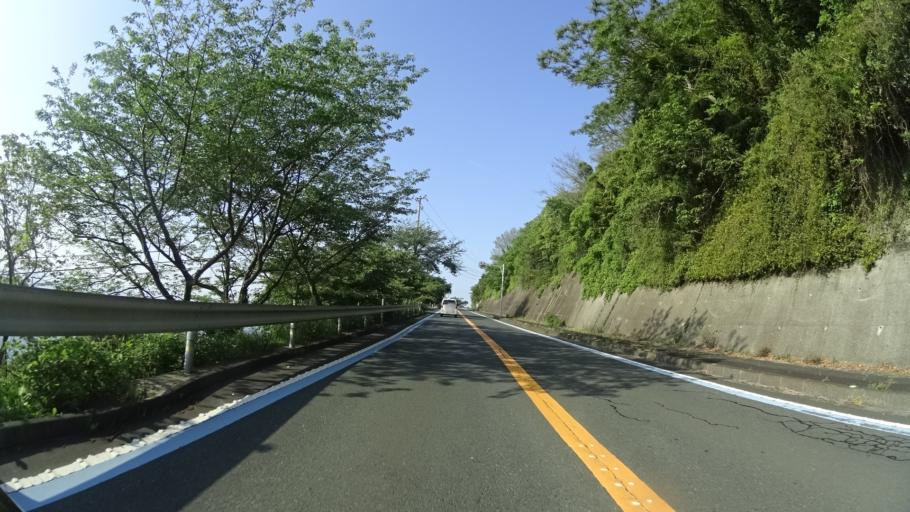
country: JP
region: Ehime
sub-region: Nishiuwa-gun
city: Ikata-cho
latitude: 33.4004
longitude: 132.1654
